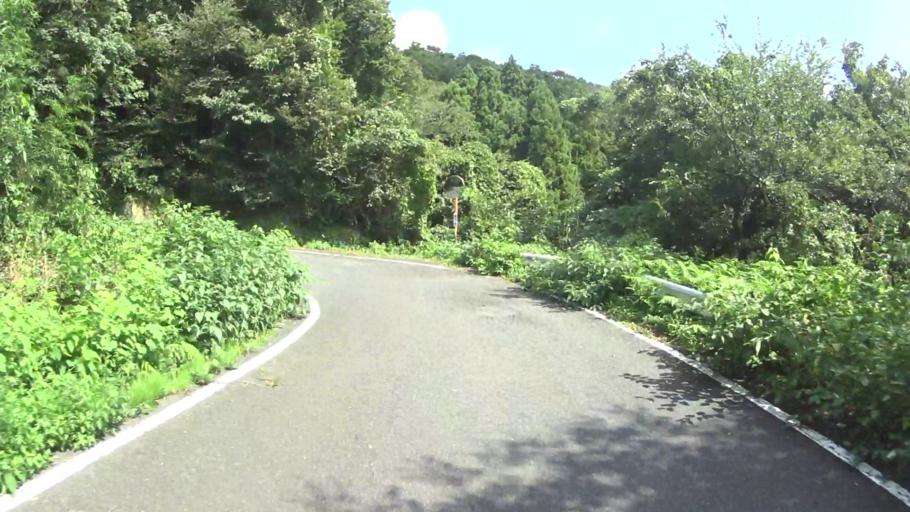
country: JP
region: Kyoto
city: Miyazu
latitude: 35.7272
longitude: 135.2103
